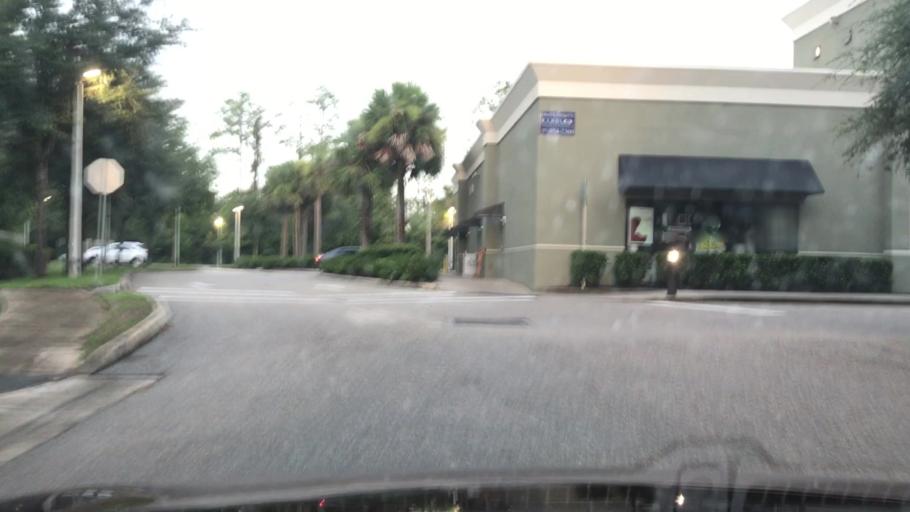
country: US
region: Florida
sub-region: Sarasota County
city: Desoto Lakes
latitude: 27.4394
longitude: -82.4507
